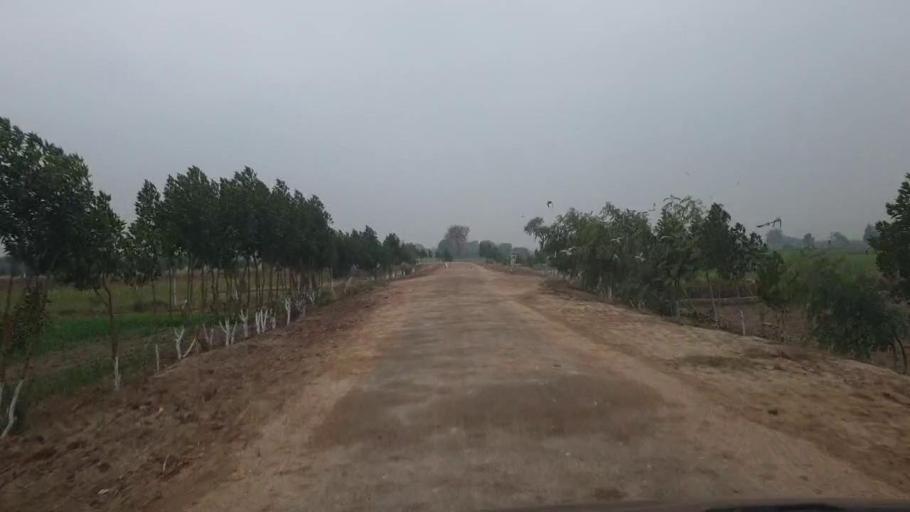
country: PK
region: Sindh
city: Tando Adam
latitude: 25.8070
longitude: 68.6708
